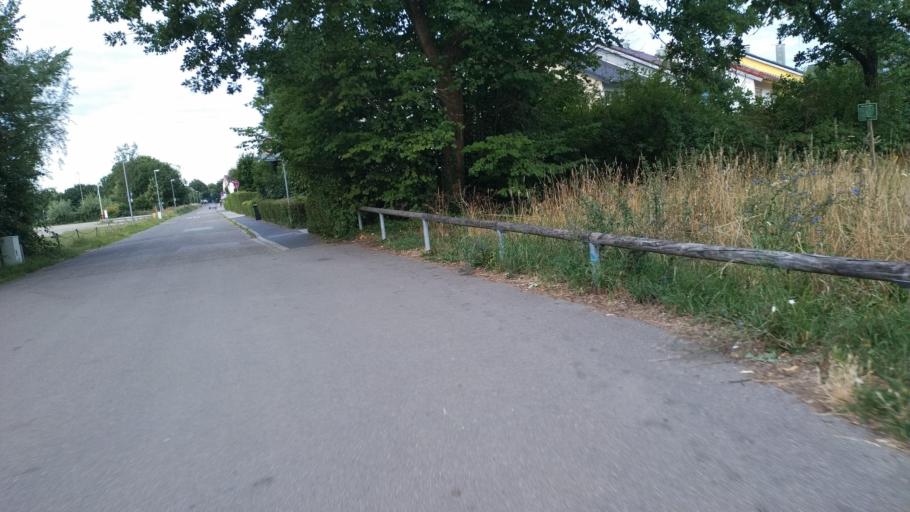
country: DE
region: Baden-Wuerttemberg
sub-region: Karlsruhe Region
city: Karlsdorf-Neuthard
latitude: 49.0941
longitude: 8.5524
